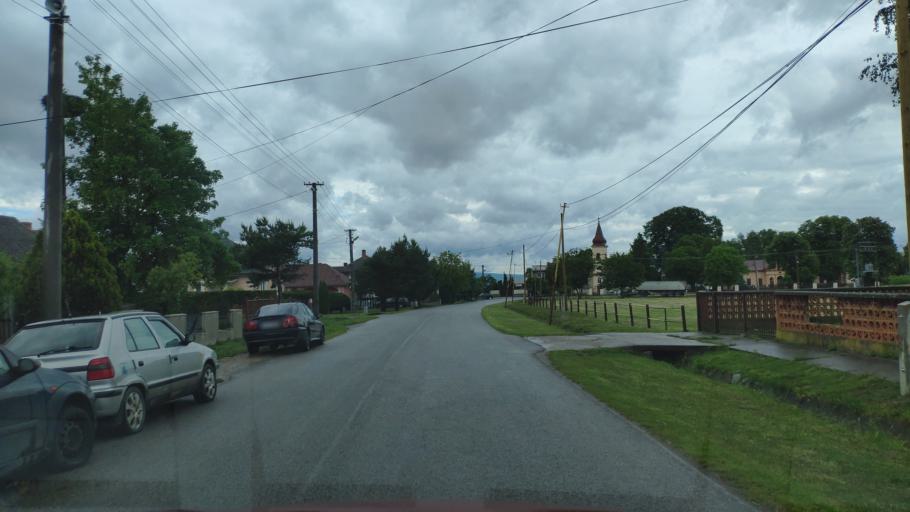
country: SK
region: Kosicky
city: Moldava nad Bodvou
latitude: 48.5381
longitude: 21.1091
